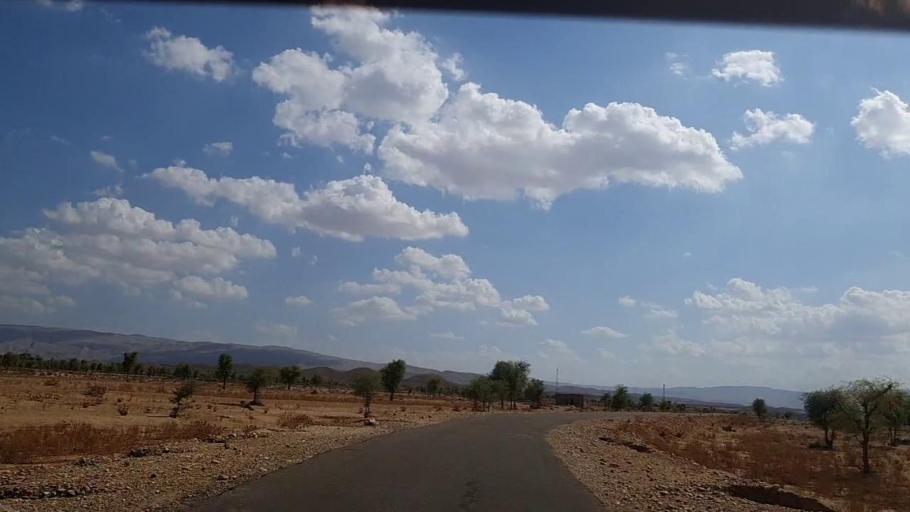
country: PK
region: Sindh
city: Johi
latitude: 26.5049
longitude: 67.4423
